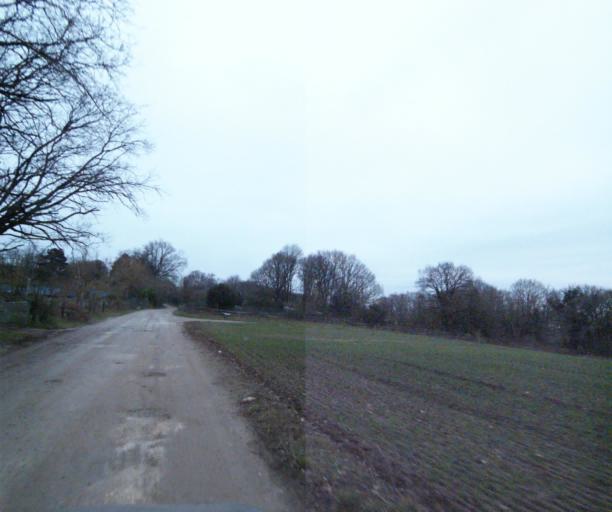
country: FR
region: Ile-de-France
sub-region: Departement de Seine-et-Marne
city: Longperrier
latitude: 49.0617
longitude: 2.6603
